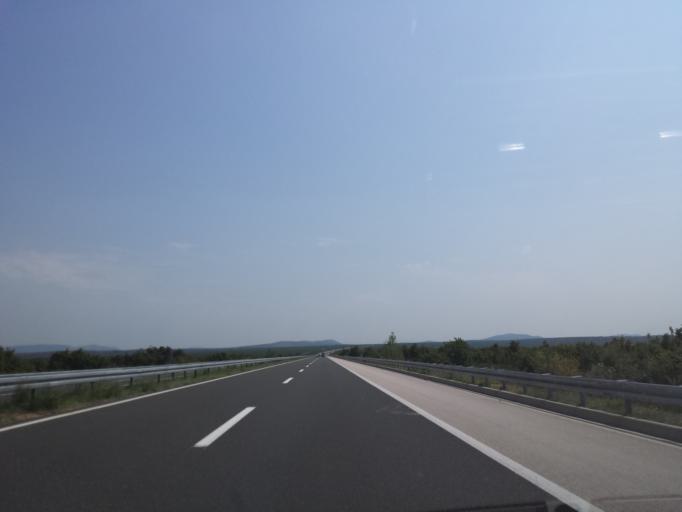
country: HR
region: Zadarska
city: Benkovac
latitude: 44.0000
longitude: 15.6050
